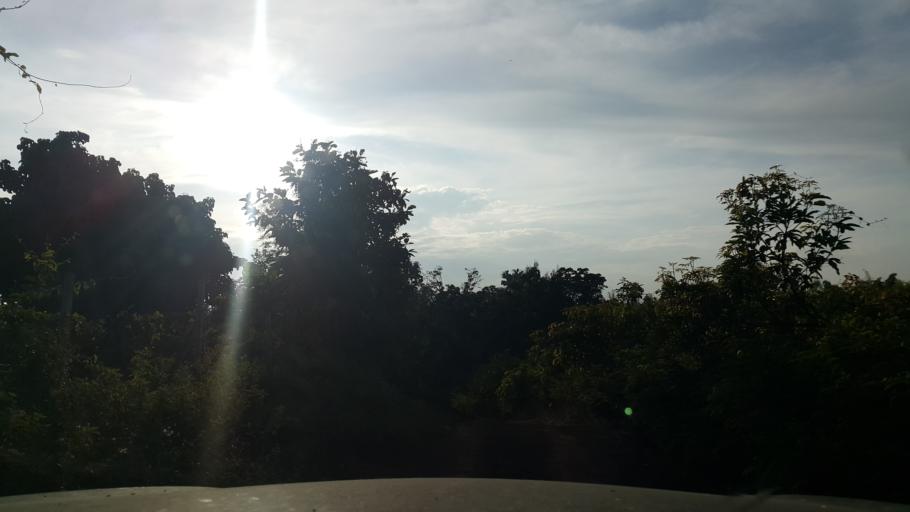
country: TH
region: Chiang Mai
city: San Sai
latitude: 18.9243
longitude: 99.0424
